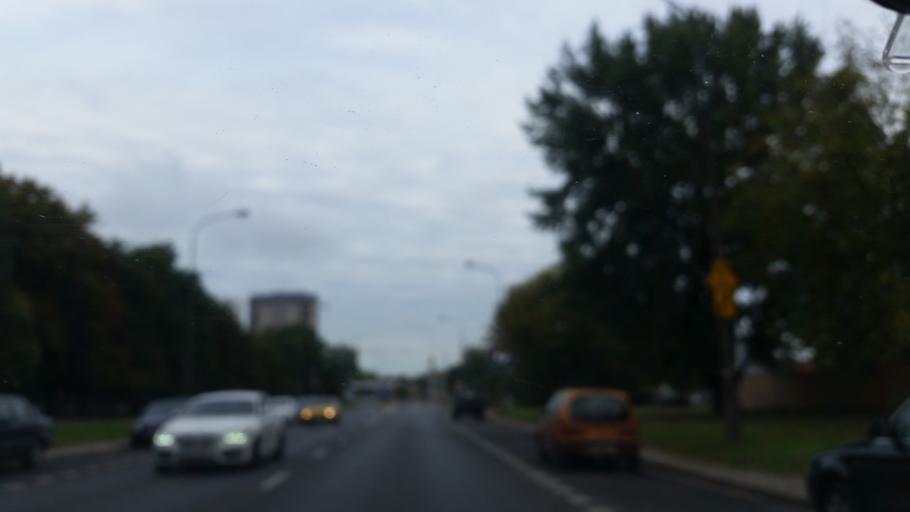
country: PL
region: Masovian Voivodeship
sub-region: Warszawa
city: Bielany
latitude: 52.2781
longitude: 20.9231
